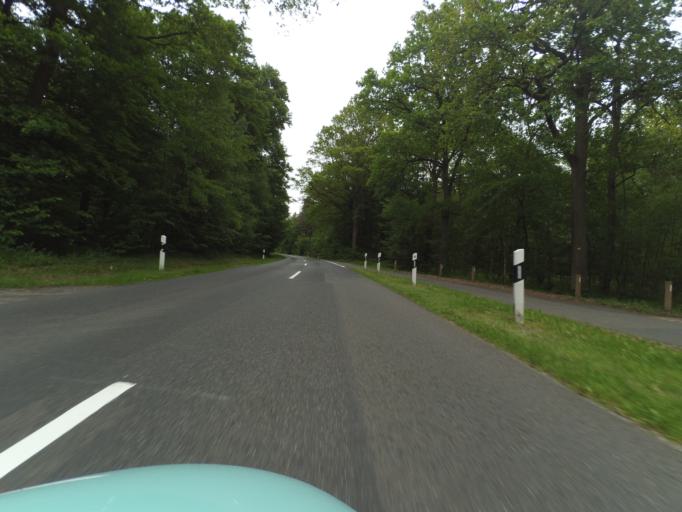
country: DE
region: Lower Saxony
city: Adenbuettel
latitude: 52.3995
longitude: 10.4652
